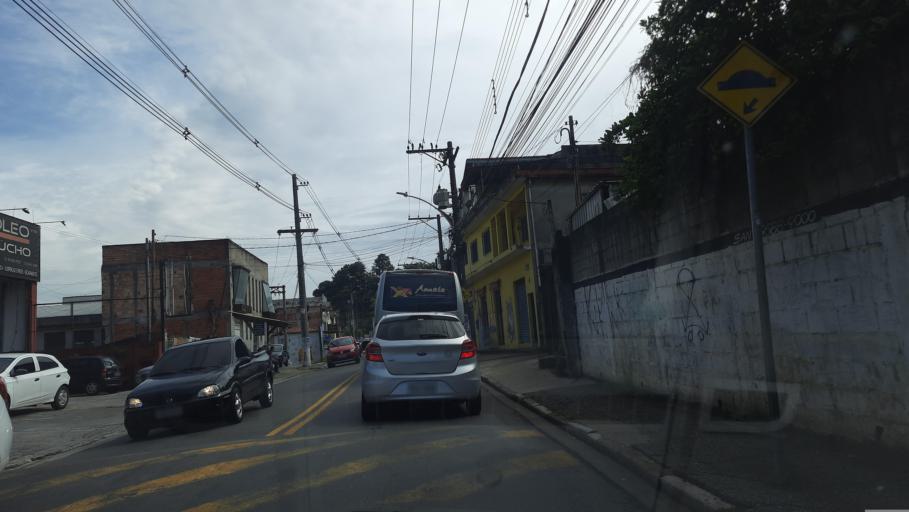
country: BR
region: Sao Paulo
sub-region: Caieiras
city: Caieiras
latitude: -23.3900
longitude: -46.7140
